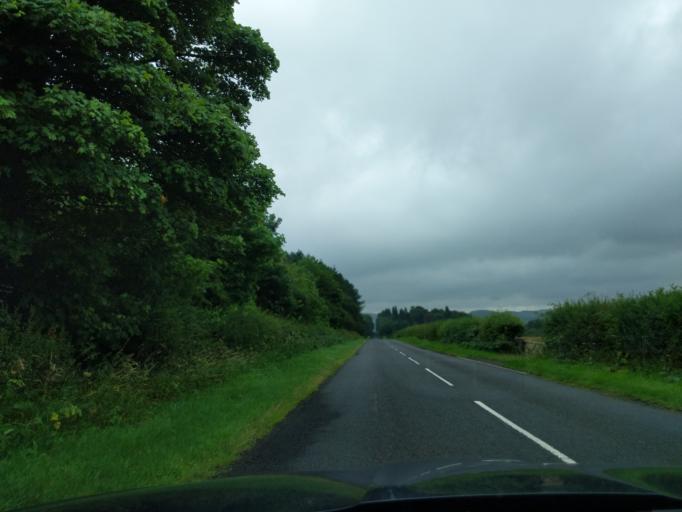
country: GB
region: England
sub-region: Northumberland
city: Ford
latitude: 55.6360
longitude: -2.0738
